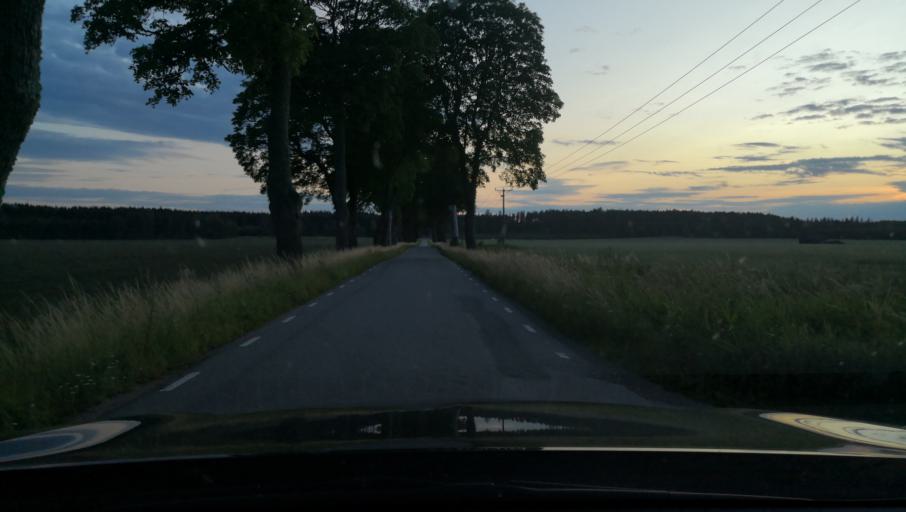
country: SE
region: Uppsala
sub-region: Osthammars Kommun
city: Bjorklinge
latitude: 60.0620
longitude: 17.5586
